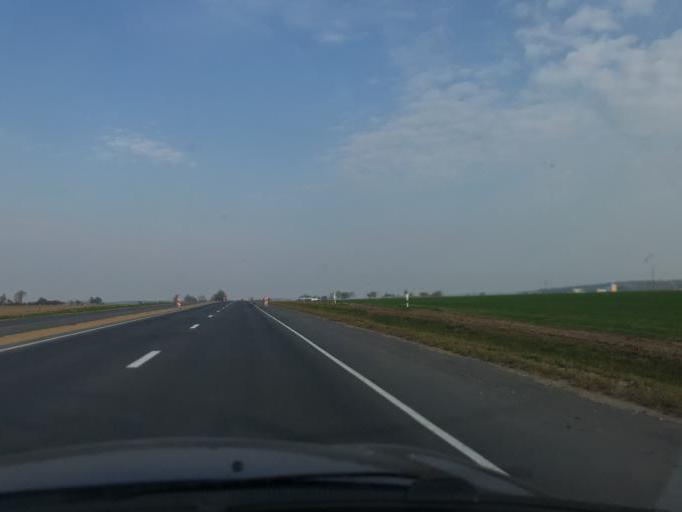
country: BY
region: Grodnenskaya
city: Shchuchin
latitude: 53.7214
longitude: 24.9643
